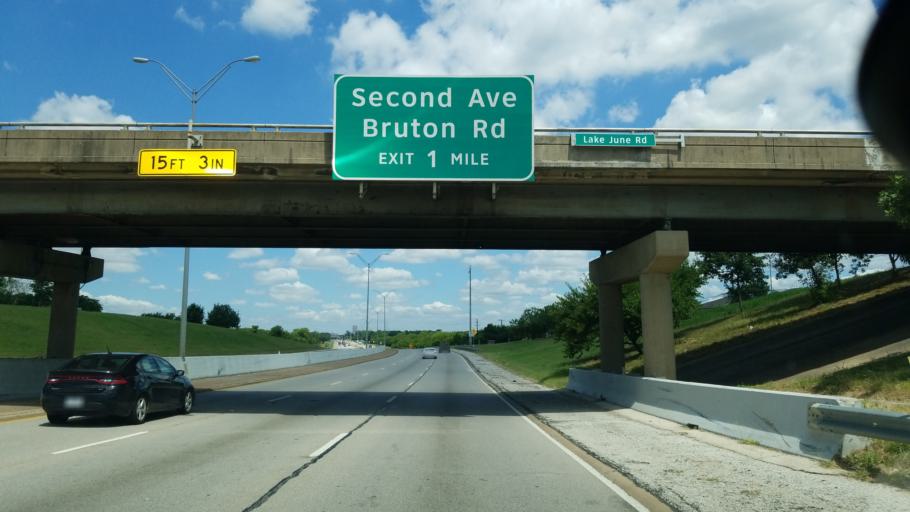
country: US
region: Texas
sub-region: Dallas County
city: Hutchins
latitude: 32.7338
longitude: -96.7128
